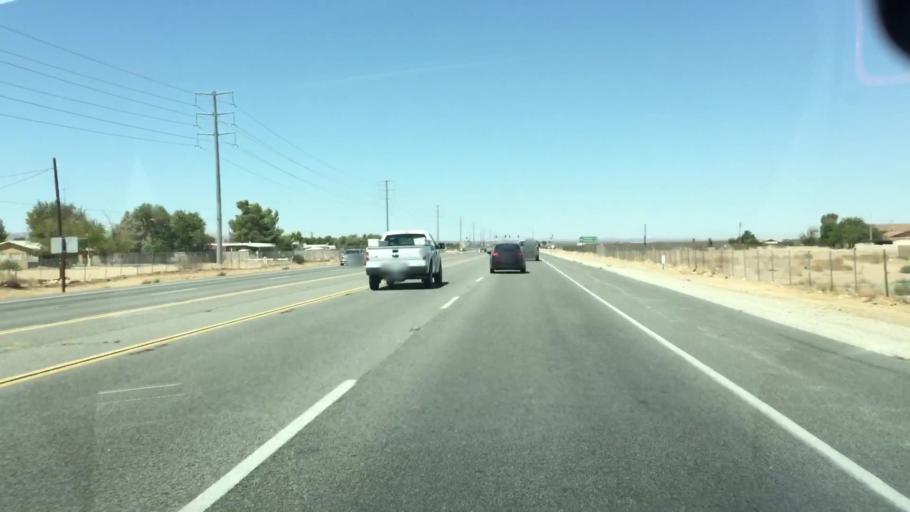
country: US
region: California
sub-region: San Bernardino County
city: Adelanto
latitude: 34.5825
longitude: -117.4131
